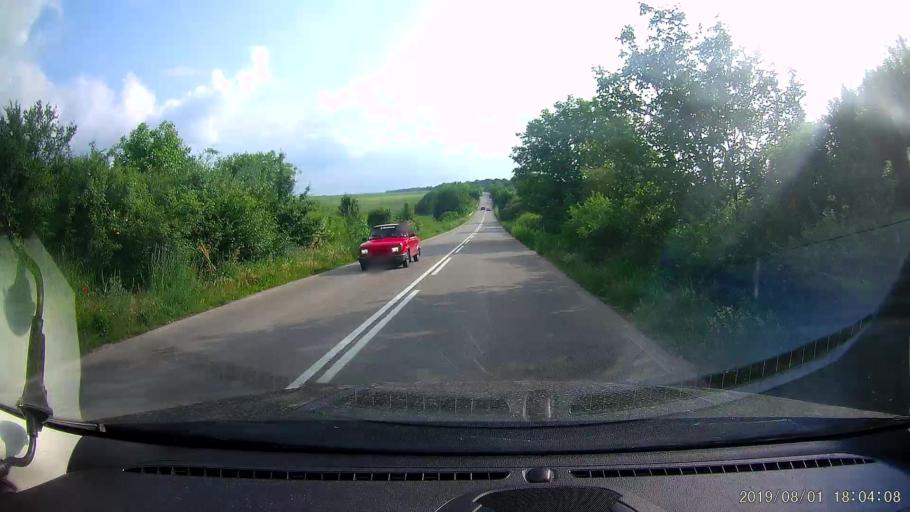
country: BG
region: Silistra
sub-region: Obshtina Alfatar
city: Alfatar
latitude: 43.9129
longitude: 27.2864
